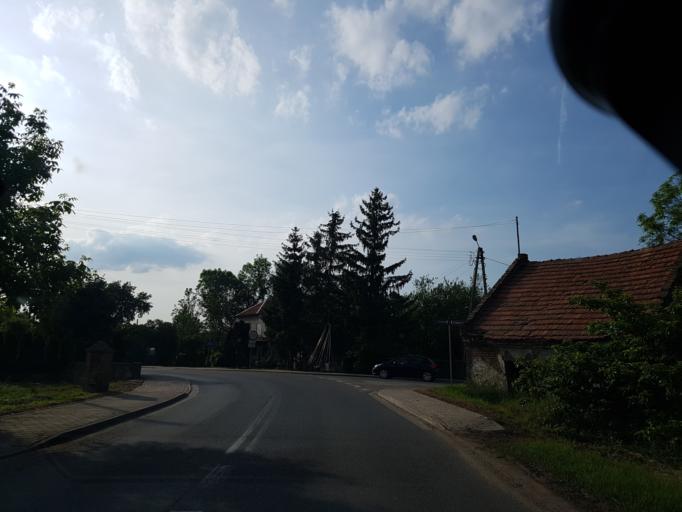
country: PL
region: Lower Silesian Voivodeship
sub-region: Powiat wroclawski
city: Kobierzyce
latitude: 50.9311
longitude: 16.9472
